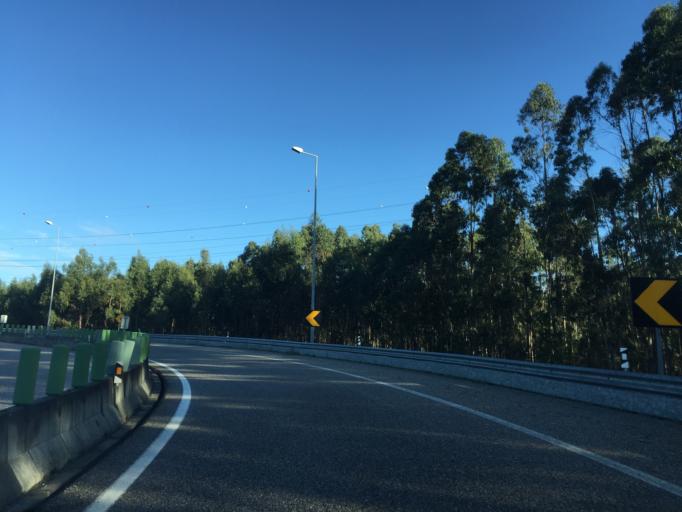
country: PT
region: Coimbra
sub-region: Figueira da Foz
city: Lavos
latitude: 40.0431
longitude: -8.8109
